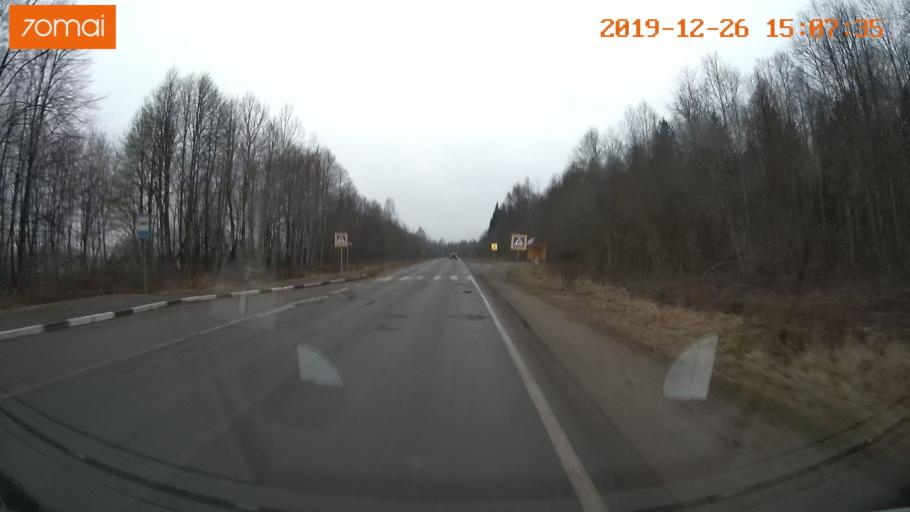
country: RU
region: Jaroslavl
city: Rybinsk
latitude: 58.1684
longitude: 38.8415
